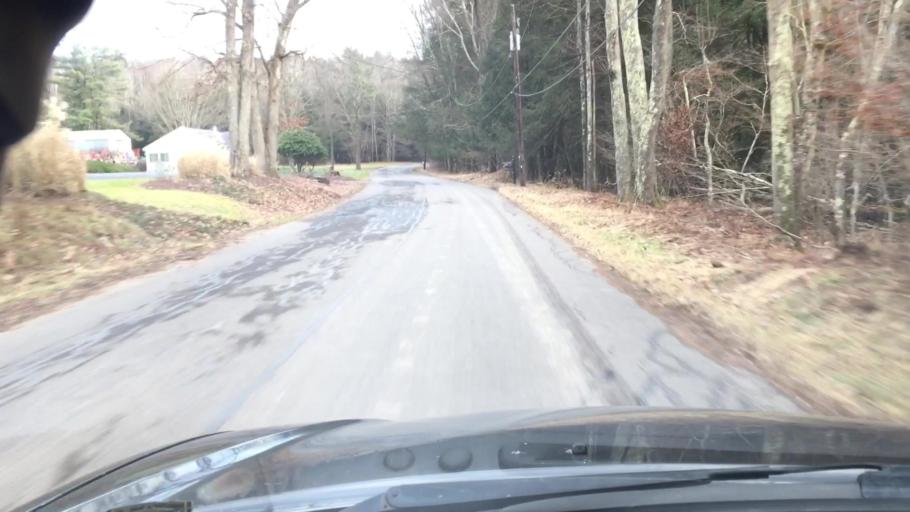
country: US
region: Pennsylvania
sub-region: Luzerne County
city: Back Mountain
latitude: 41.3102
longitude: -76.0625
